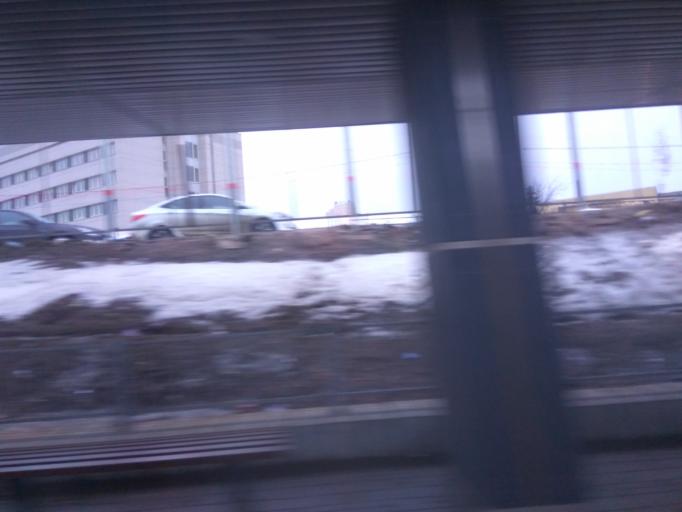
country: RU
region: Moscow
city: Mar'ina Roshcha
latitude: 55.7937
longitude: 37.6384
